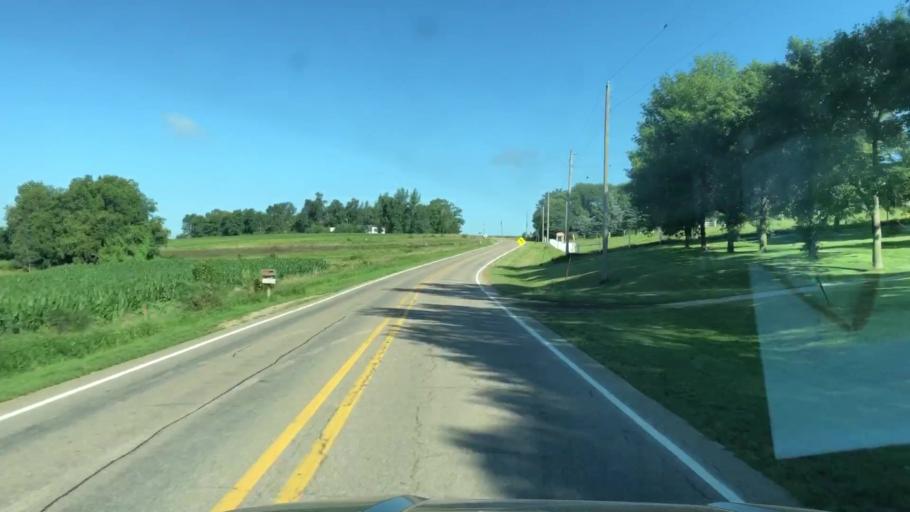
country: US
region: Iowa
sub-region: Woodbury County
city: Sergeant Bluff
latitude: 42.4232
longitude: -96.2756
